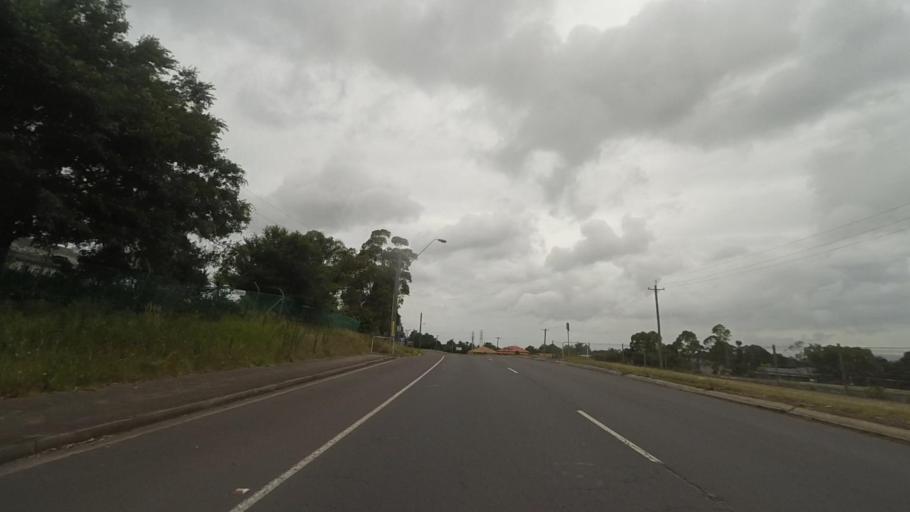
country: AU
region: New South Wales
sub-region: Wollongong
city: Berkeley
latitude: -34.4692
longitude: 150.8271
